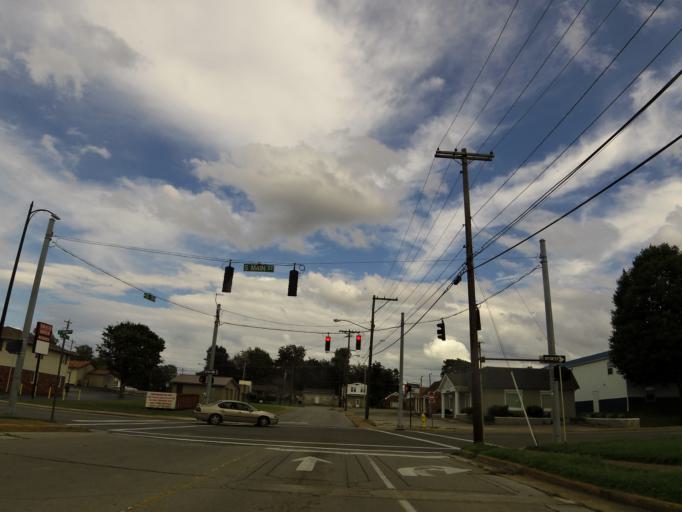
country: US
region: Kentucky
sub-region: Christian County
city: Hopkinsville
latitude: 36.8702
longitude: -87.4861
